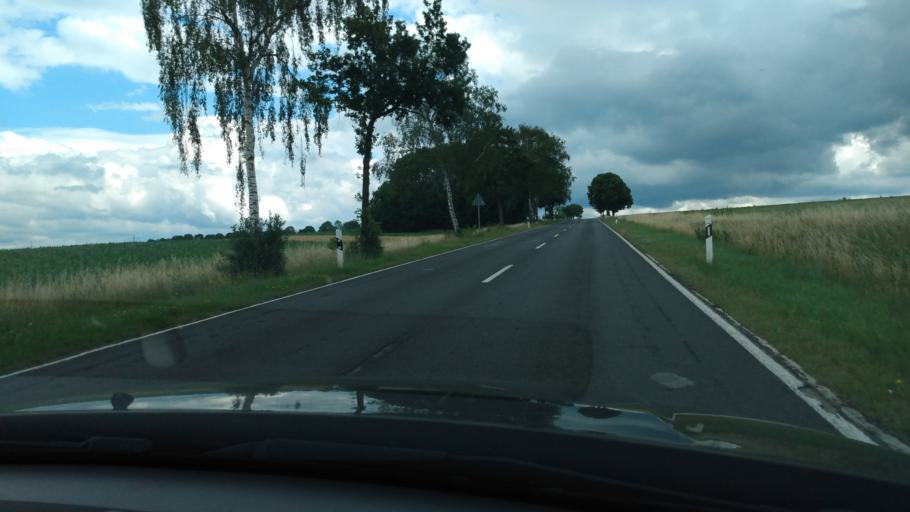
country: DE
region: Rheinland-Pfalz
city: Musweiler
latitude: 50.0192
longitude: 6.8062
